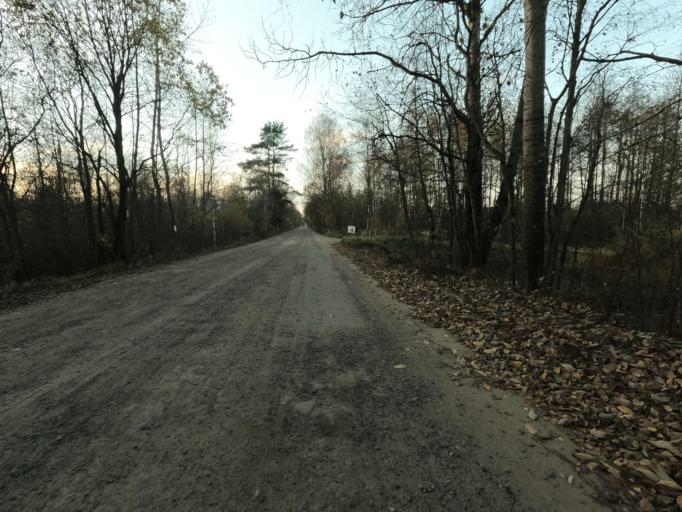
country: RU
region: Leningrad
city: Mga
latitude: 59.7628
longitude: 31.2539
